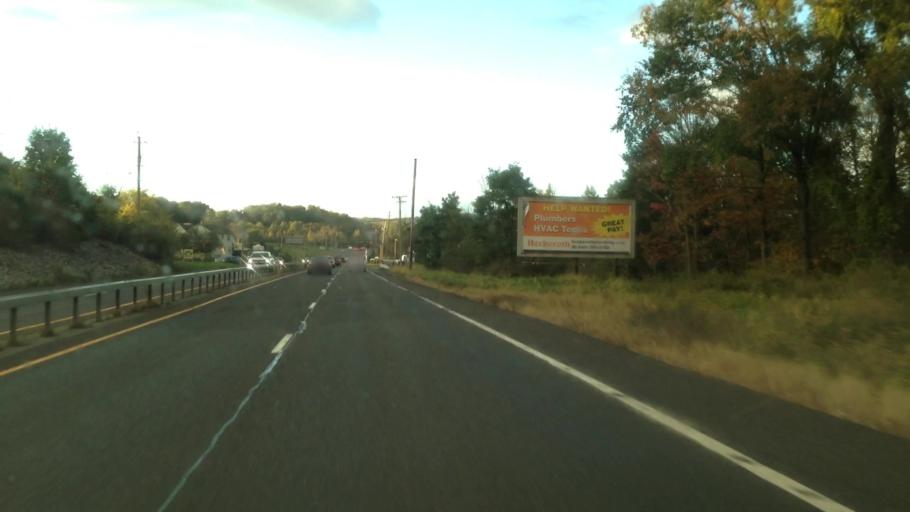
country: US
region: New York
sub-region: Ulster County
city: Highland
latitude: 41.7358
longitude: -73.9613
